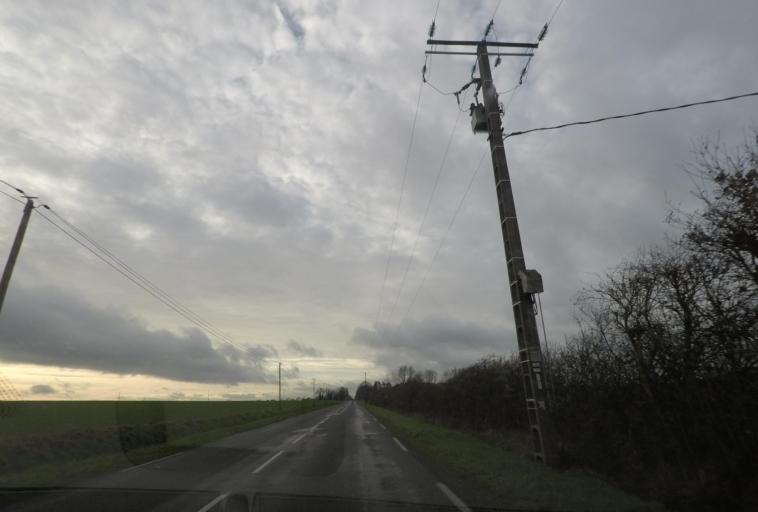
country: FR
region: Pays de la Loire
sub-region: Departement de la Sarthe
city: Saint-Calais
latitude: 47.9525
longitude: 0.7540
